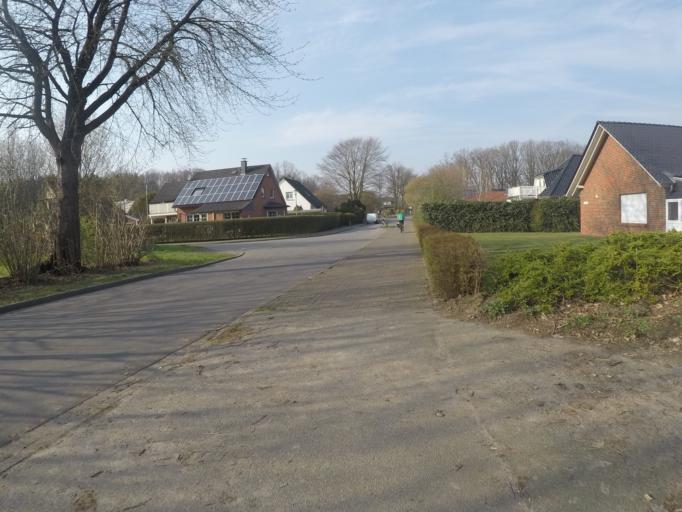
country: DE
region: Schleswig-Holstein
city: Wittenborn
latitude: 53.9202
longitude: 10.2214
